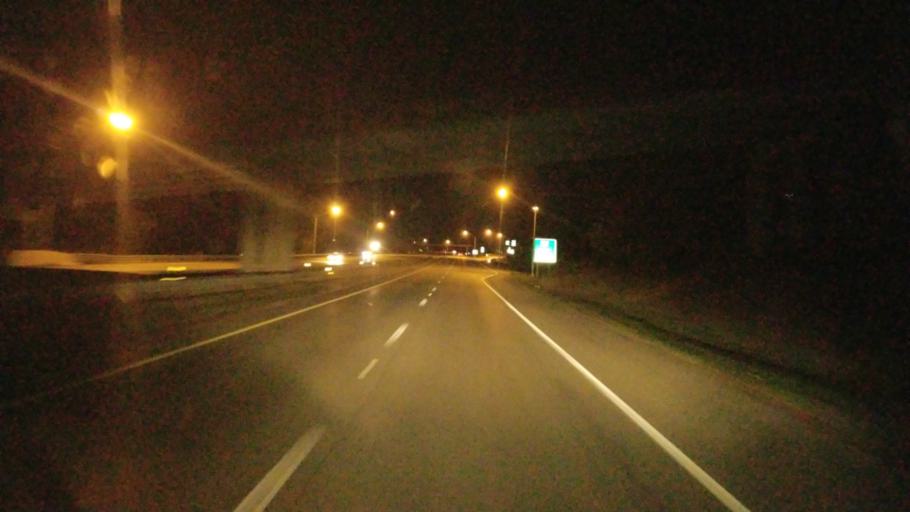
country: US
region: Ohio
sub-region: Hocking County
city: Logan
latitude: 39.5354
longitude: -82.4357
